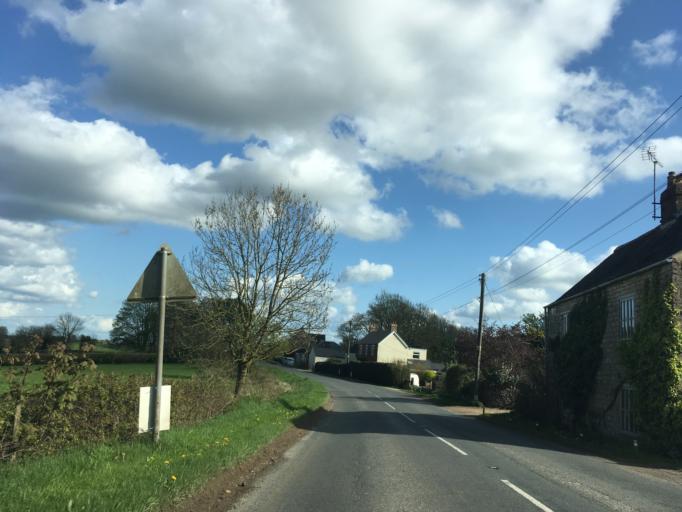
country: GB
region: England
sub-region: Gloucestershire
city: Stonehouse
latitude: 51.7006
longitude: -2.2931
